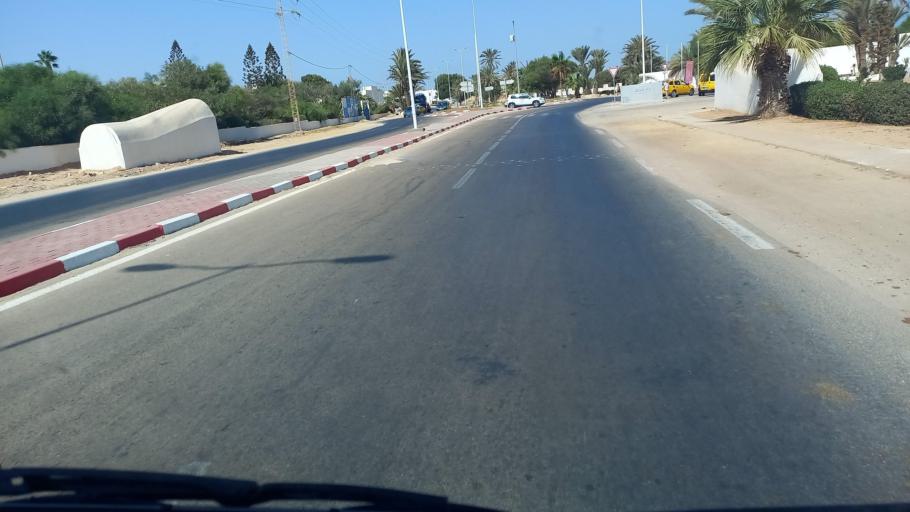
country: TN
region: Madanin
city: Midoun
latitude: 33.8269
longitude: 11.0325
